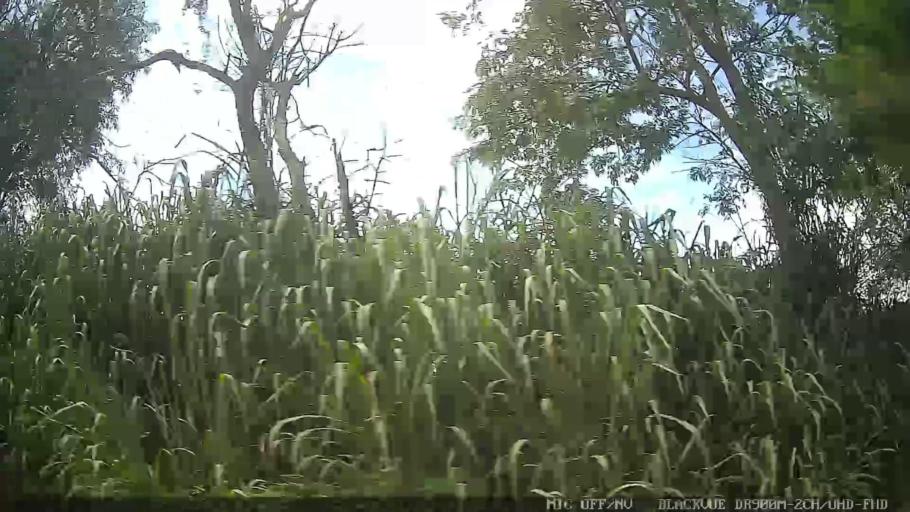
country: BR
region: Sao Paulo
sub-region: Aruja
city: Aruja
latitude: -23.4257
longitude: -46.2338
